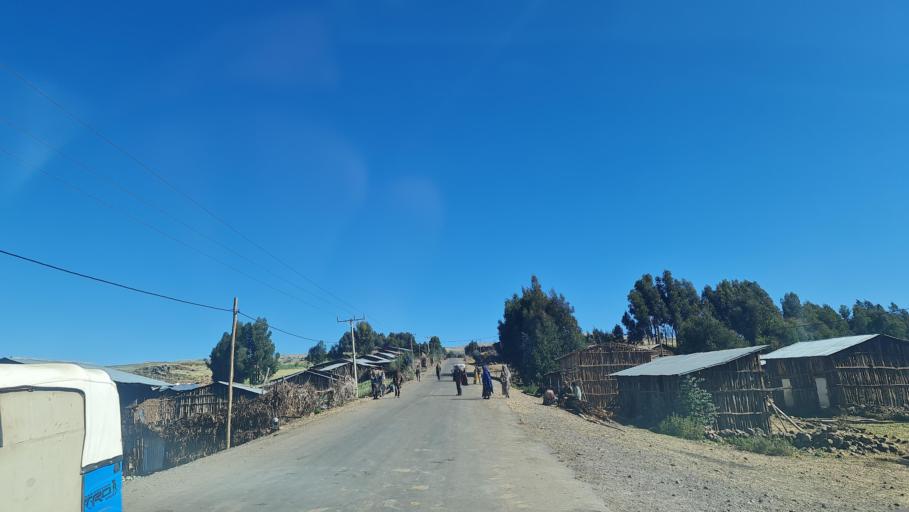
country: ET
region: Amhara
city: Debark'
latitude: 13.1011
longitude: 38.1434
